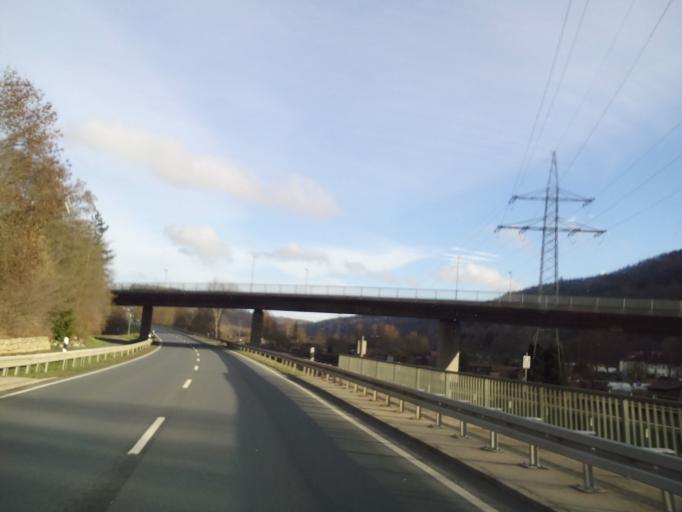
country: DE
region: Bavaria
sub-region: Upper Franconia
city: Kulmbach
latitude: 50.1124
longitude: 11.4649
